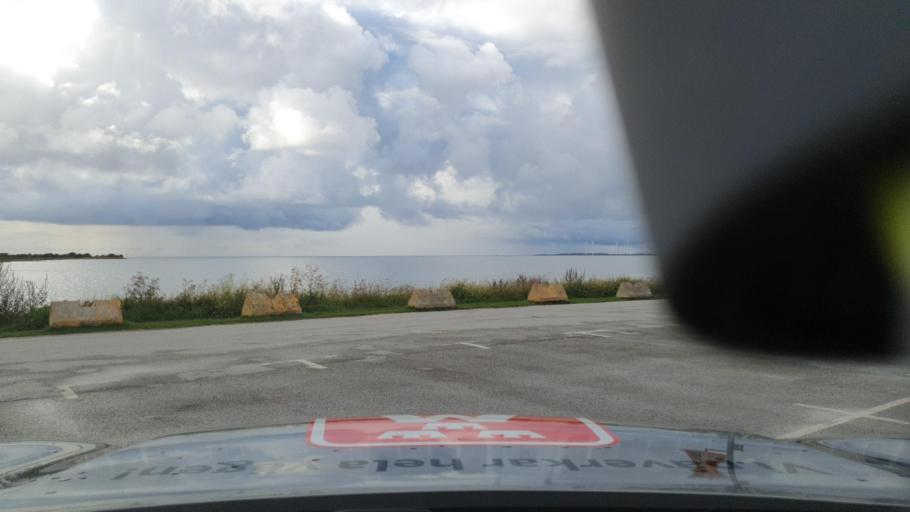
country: SE
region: Gotland
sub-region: Gotland
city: Hemse
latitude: 57.0338
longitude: 18.2584
